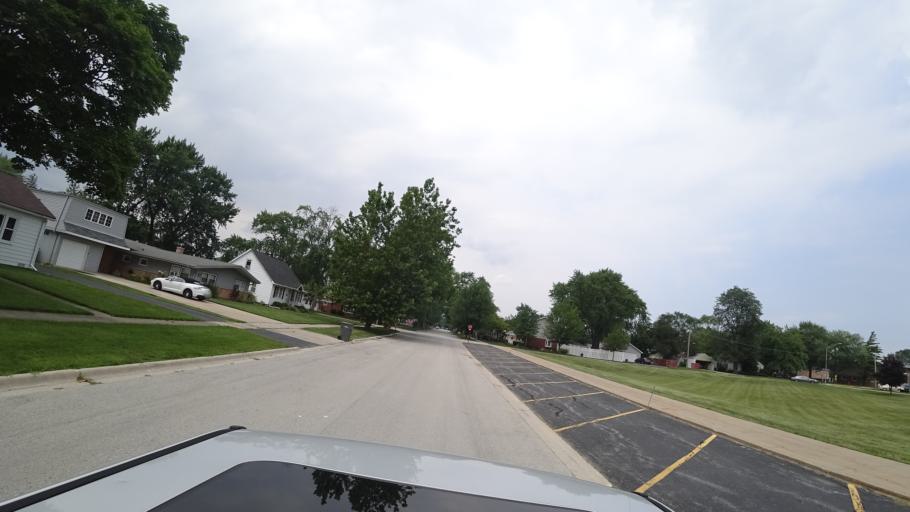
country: US
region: Illinois
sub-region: Cook County
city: Chicago Ridge
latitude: 41.6953
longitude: -87.7741
